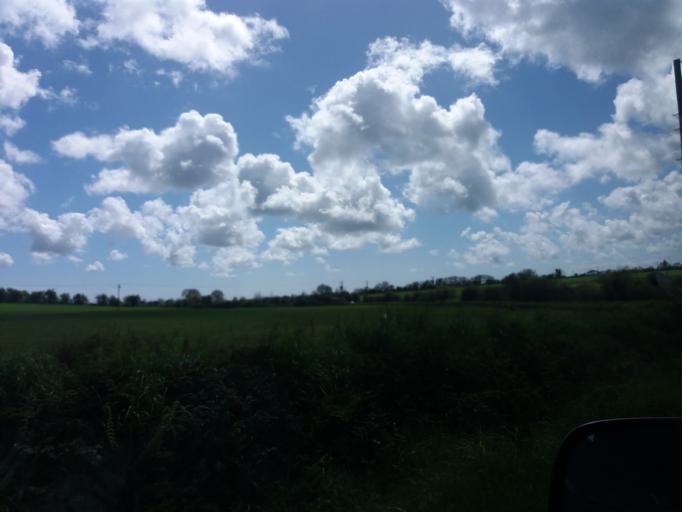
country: IE
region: Munster
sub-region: Waterford
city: Dunmore East
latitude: 52.2423
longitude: -7.0067
